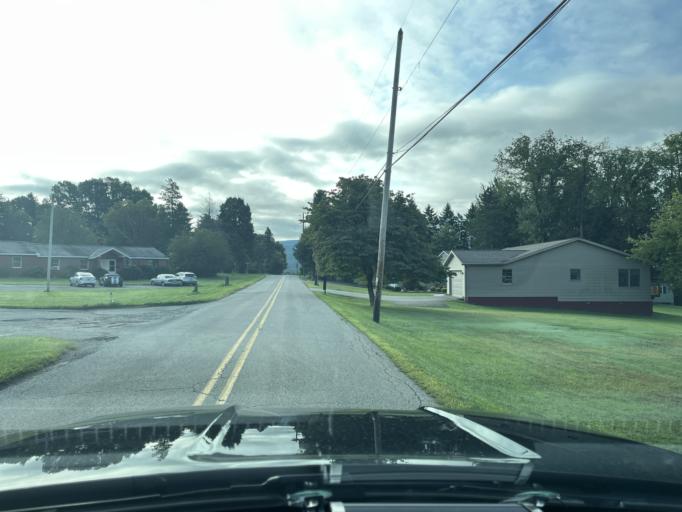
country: US
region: Pennsylvania
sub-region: Fayette County
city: Leith-Hatfield
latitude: 39.8702
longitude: -79.7390
